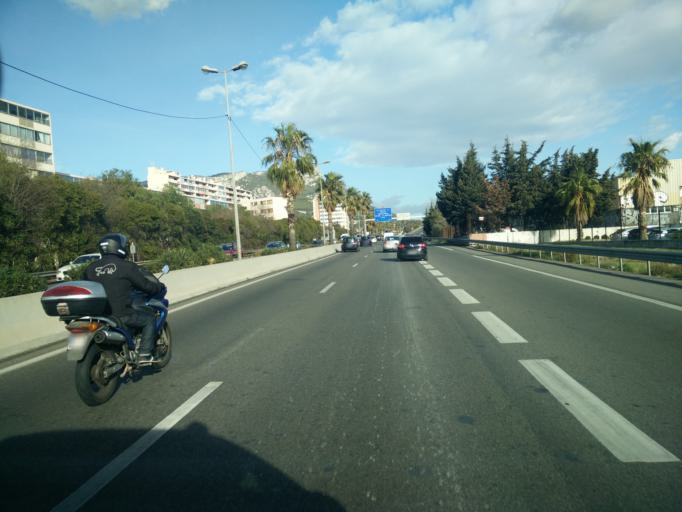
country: FR
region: Provence-Alpes-Cote d'Azur
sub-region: Departement du Var
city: La Valette-du-Var
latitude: 43.1290
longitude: 5.9771
